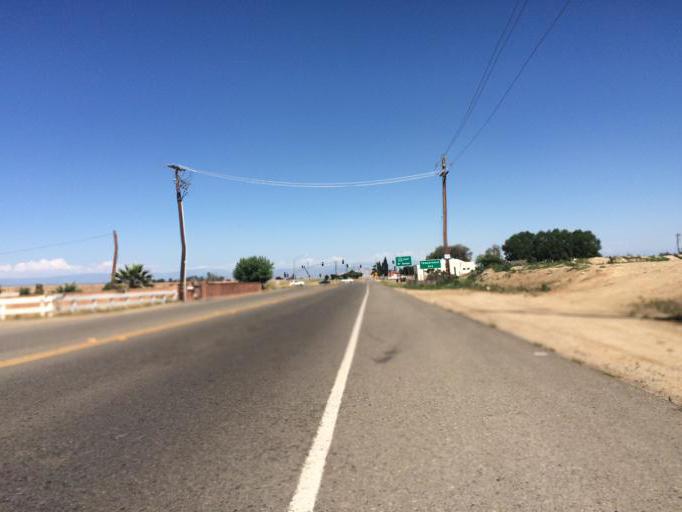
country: US
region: California
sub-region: Fresno County
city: Sunnyside
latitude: 36.7369
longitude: -119.6667
